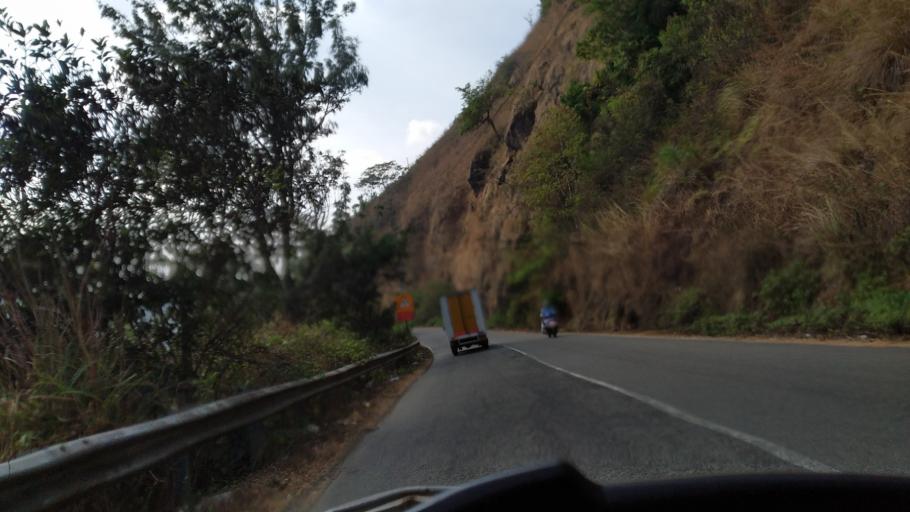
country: IN
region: Kerala
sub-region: Kottayam
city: Erattupetta
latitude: 9.5678
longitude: 77.0075
